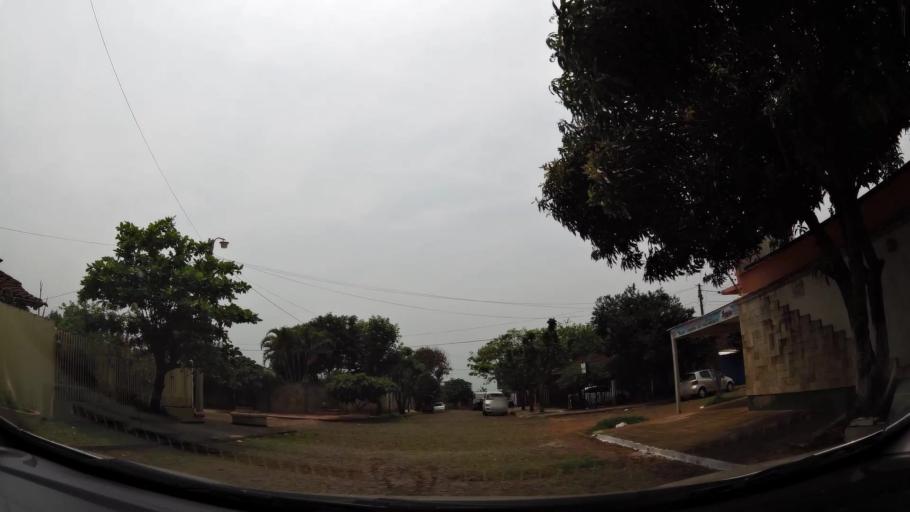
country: PY
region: Alto Parana
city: Presidente Franco
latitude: -25.5554
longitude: -54.6241
